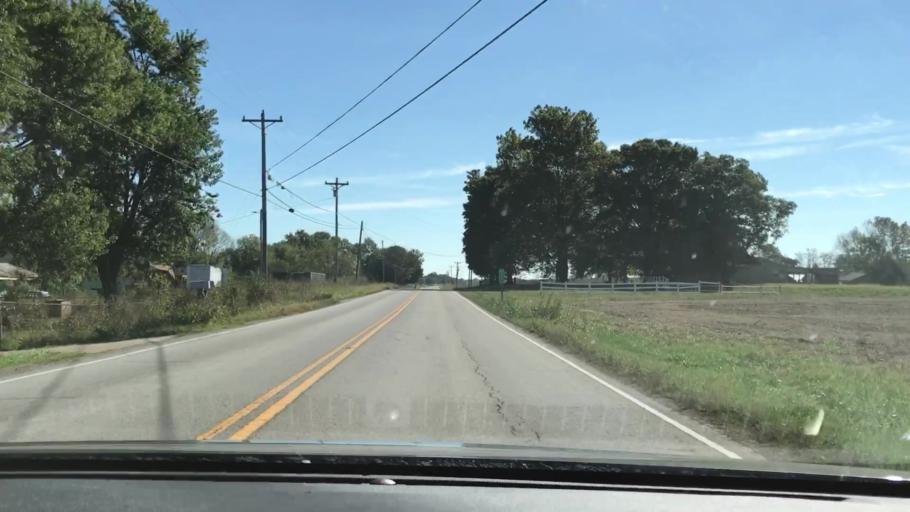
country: US
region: Kentucky
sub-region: Christian County
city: Hopkinsville
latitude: 36.8622
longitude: -87.4413
